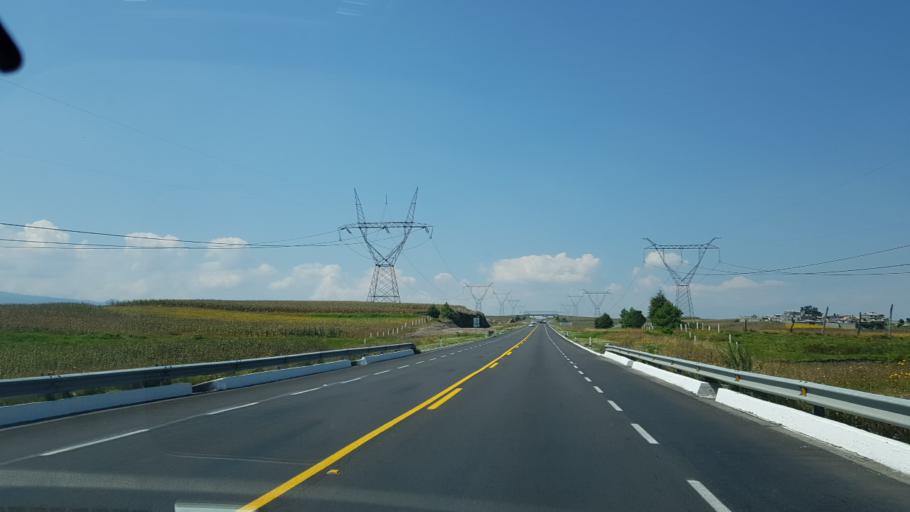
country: MX
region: Mexico
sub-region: Almoloya de Juarez
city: Conjunto Habitacional Ecologico SUTEYM
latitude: 19.3845
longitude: -99.7709
